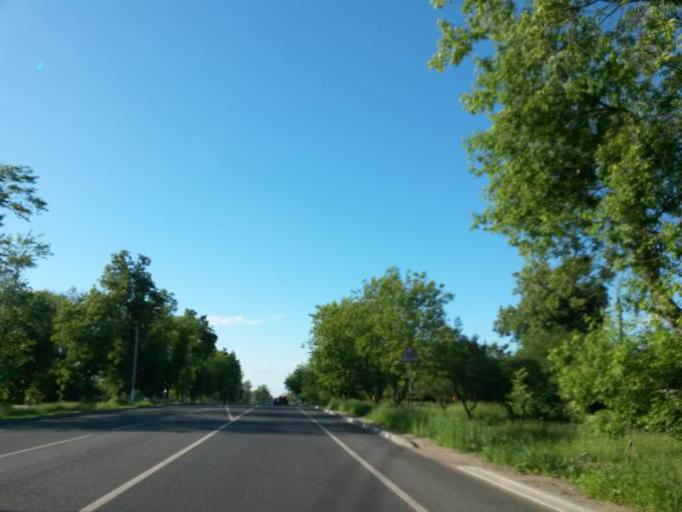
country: RU
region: Moskovskaya
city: L'vovskiy
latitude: 55.3203
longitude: 37.5287
